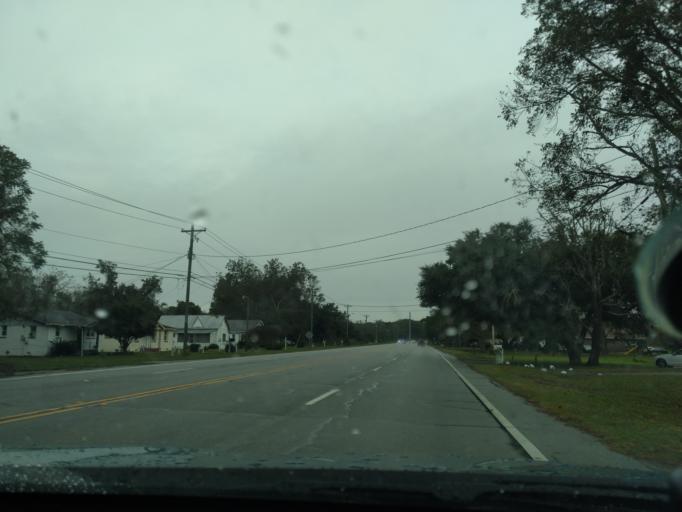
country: US
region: South Carolina
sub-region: Charleston County
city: Folly Beach
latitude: 32.6942
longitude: -79.9656
